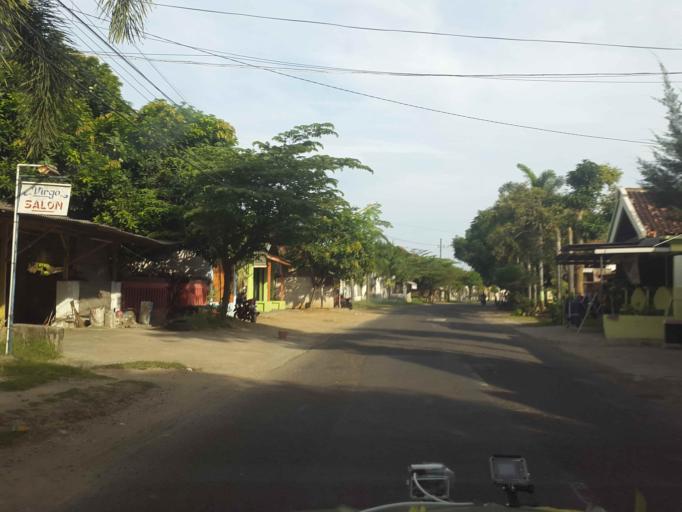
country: ID
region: East Java
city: Pasarkayu
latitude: -7.0310
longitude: 113.8888
